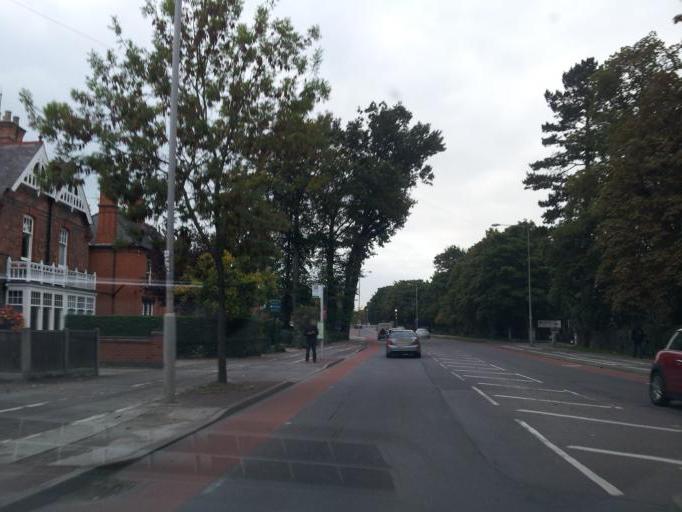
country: GB
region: England
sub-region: Nottinghamshire
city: Newark on Trent
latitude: 53.0655
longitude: -0.7922
